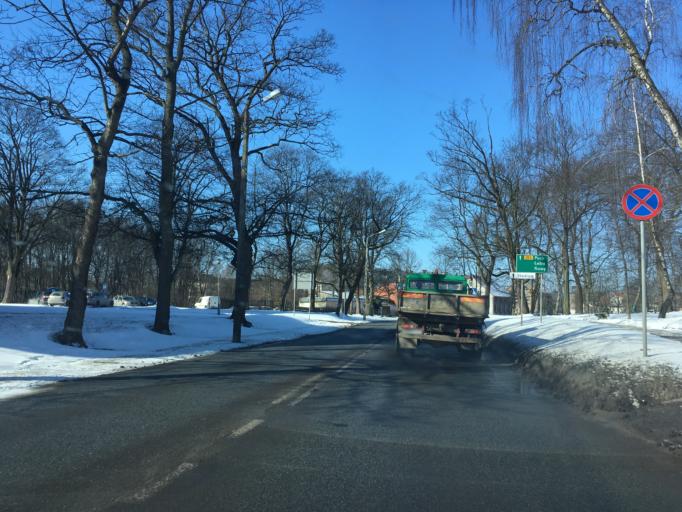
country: PL
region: Pomeranian Voivodeship
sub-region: Slupsk
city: Slupsk
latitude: 54.4691
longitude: 17.0411
